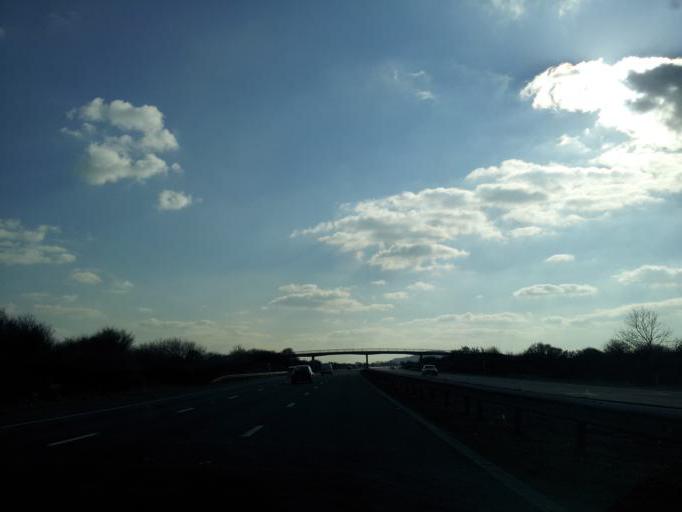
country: GB
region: England
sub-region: North Somerset
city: Hutton
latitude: 51.2890
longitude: -2.8989
